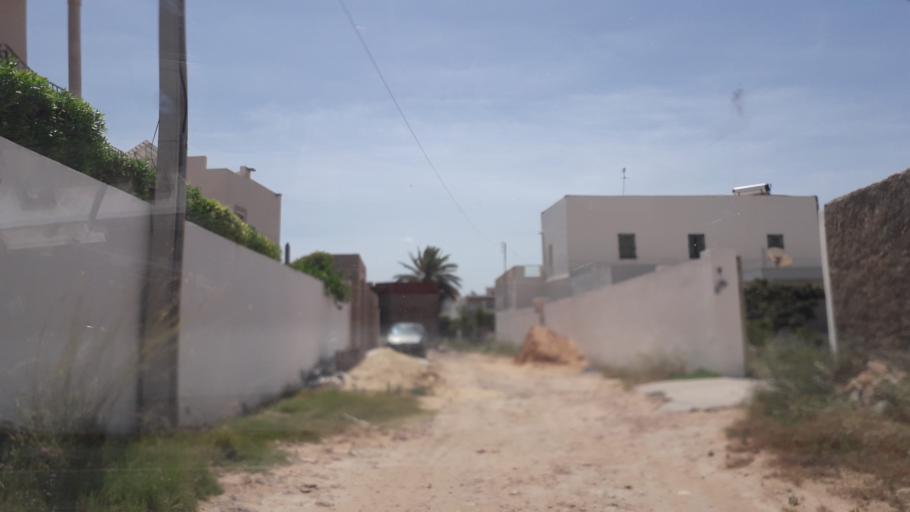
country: TN
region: Safaqis
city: Al Qarmadah
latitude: 34.8053
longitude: 10.7703
